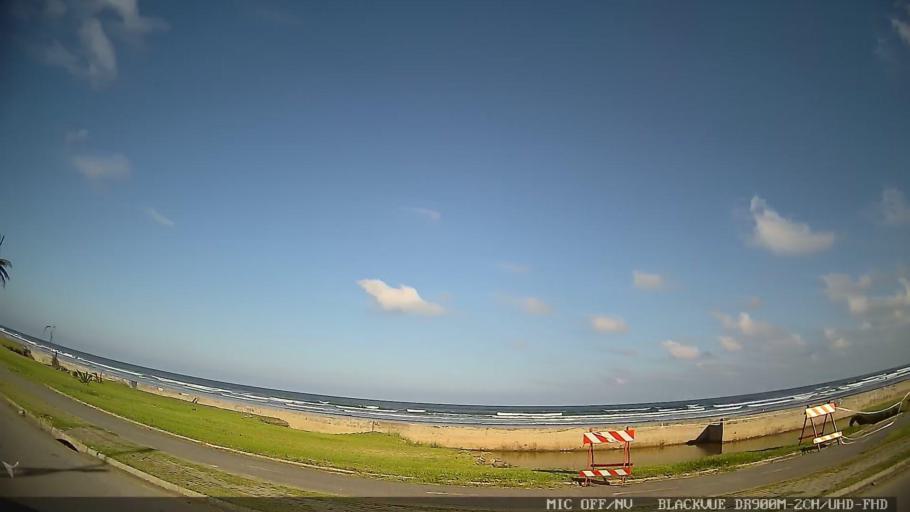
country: BR
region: Sao Paulo
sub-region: Peruibe
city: Peruibe
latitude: -24.2939
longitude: -46.9605
